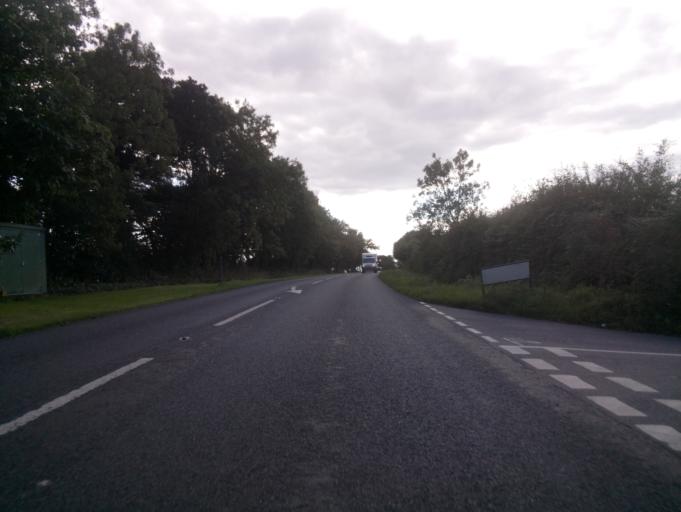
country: GB
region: England
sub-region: Devon
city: Topsham
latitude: 50.7050
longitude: -3.3871
